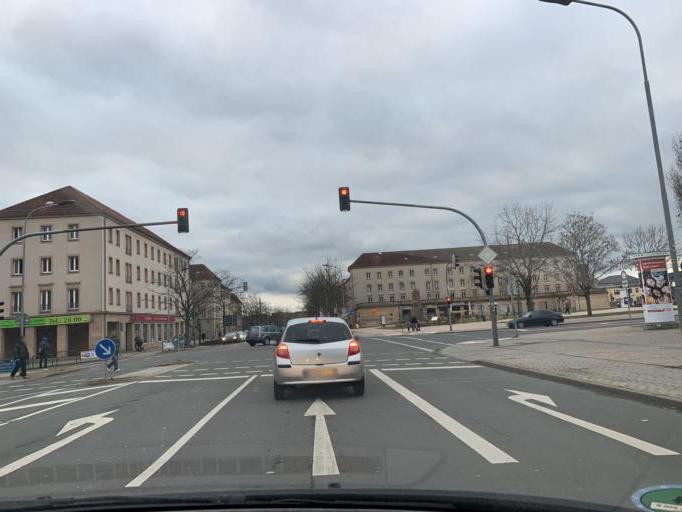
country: DE
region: Saxony-Anhalt
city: Merseburg
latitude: 51.3569
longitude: 11.9922
